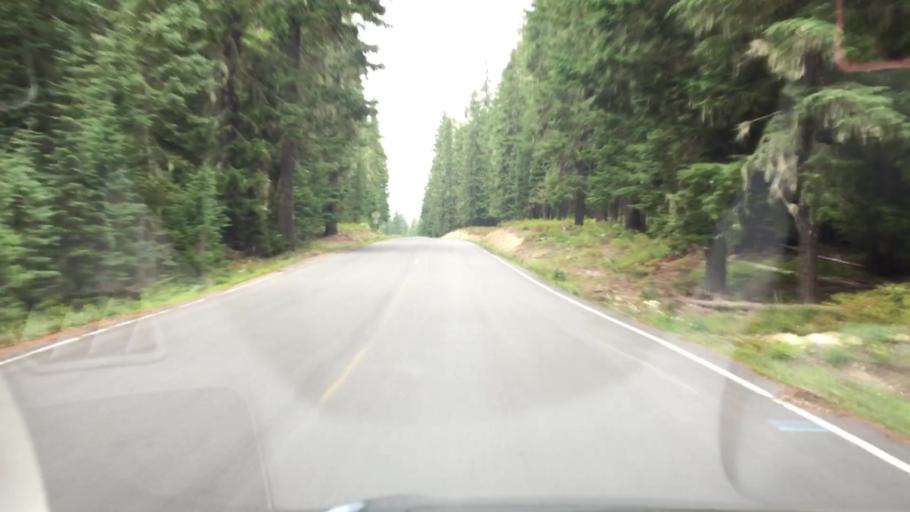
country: US
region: Washington
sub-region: Klickitat County
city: White Salmon
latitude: 46.1985
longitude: -121.6446
